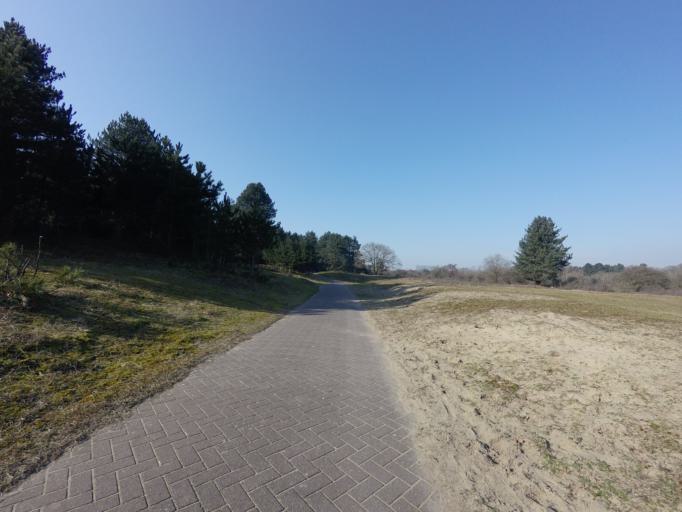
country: NL
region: North Holland
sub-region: Gemeente Bloemendaal
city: Bloemendaal
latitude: 52.4392
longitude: 4.6107
